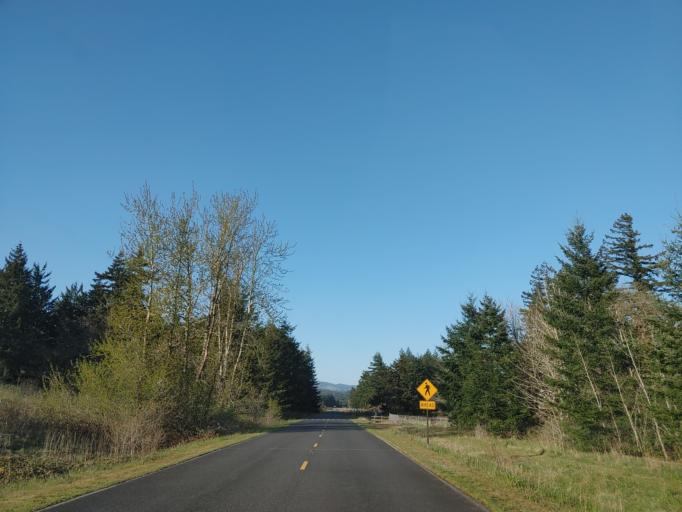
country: US
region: Oregon
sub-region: Hood River County
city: Cascade Locks
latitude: 45.6362
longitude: -121.9684
